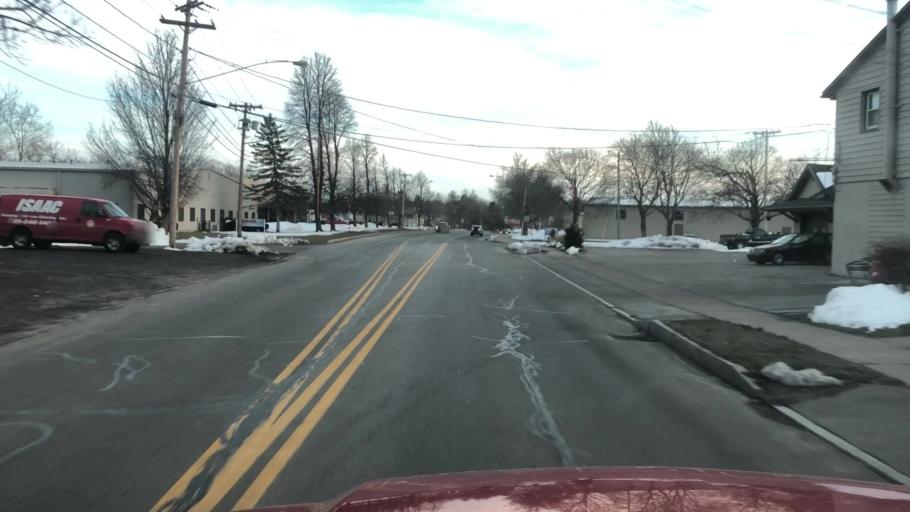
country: US
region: New York
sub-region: Monroe County
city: East Rochester
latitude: 43.1169
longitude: -77.4786
